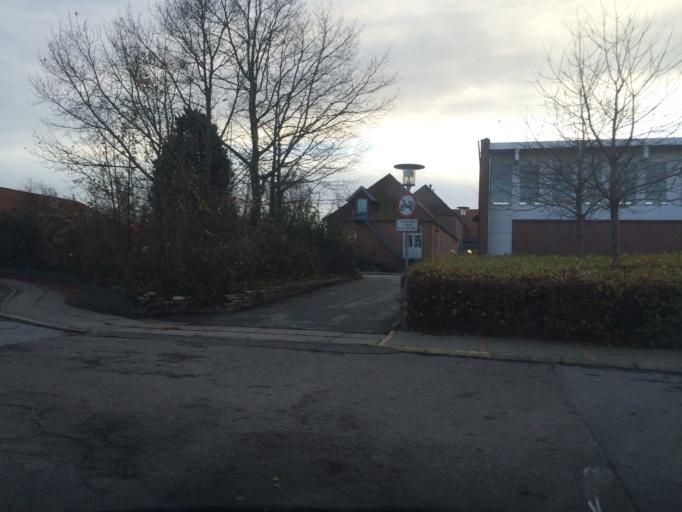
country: DK
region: South Denmark
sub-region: Sonderborg Kommune
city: Augustenborg
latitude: 54.9478
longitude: 9.8730
